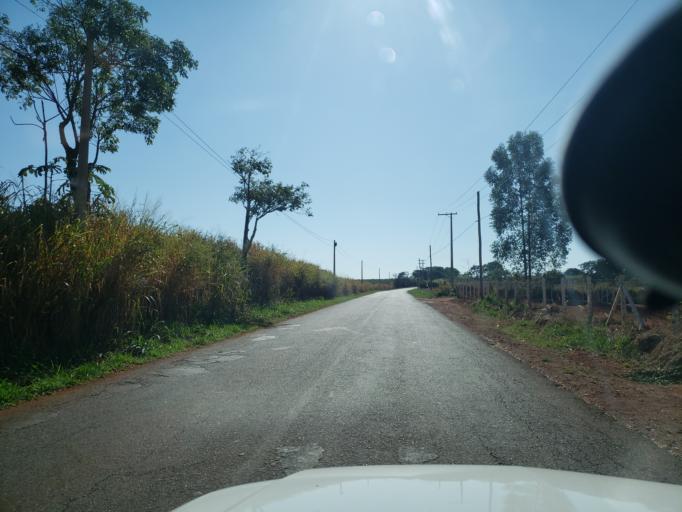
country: BR
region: Sao Paulo
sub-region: Moji-Guacu
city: Mogi-Gaucu
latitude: -22.3458
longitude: -46.8920
